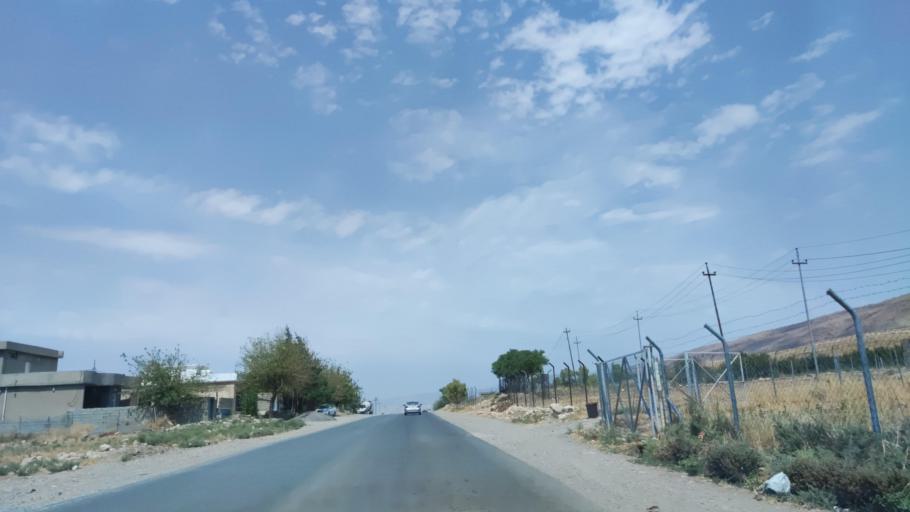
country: IQ
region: Arbil
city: Shaqlawah
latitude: 36.5277
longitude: 44.3607
